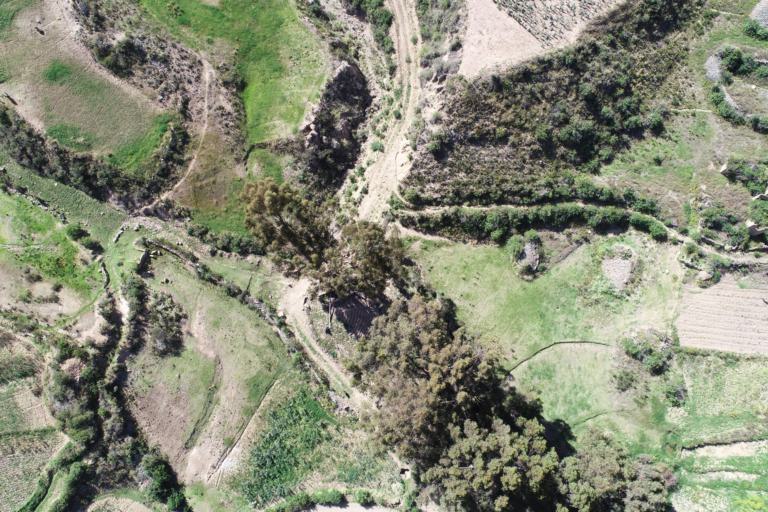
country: BO
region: La Paz
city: La Paz
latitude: -16.5536
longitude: -67.9878
